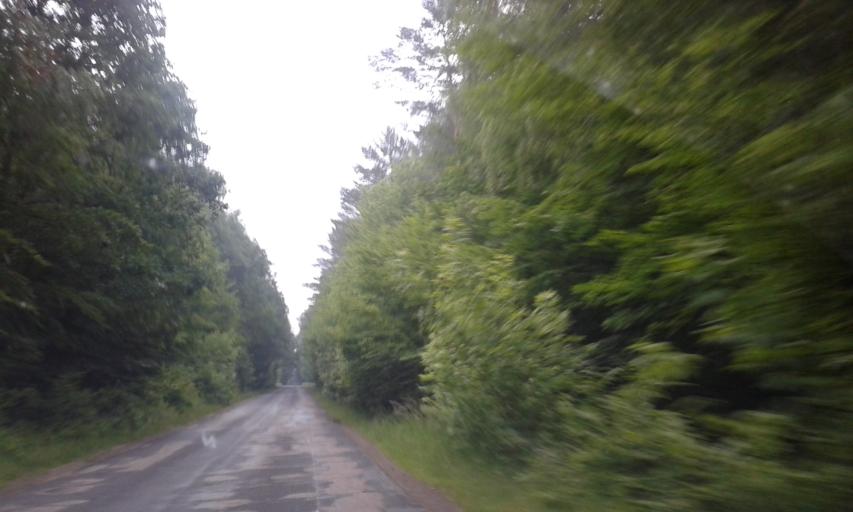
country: PL
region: Kujawsko-Pomorskie
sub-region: Powiat sepolenski
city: Sypniewo
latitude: 53.4519
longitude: 17.3585
